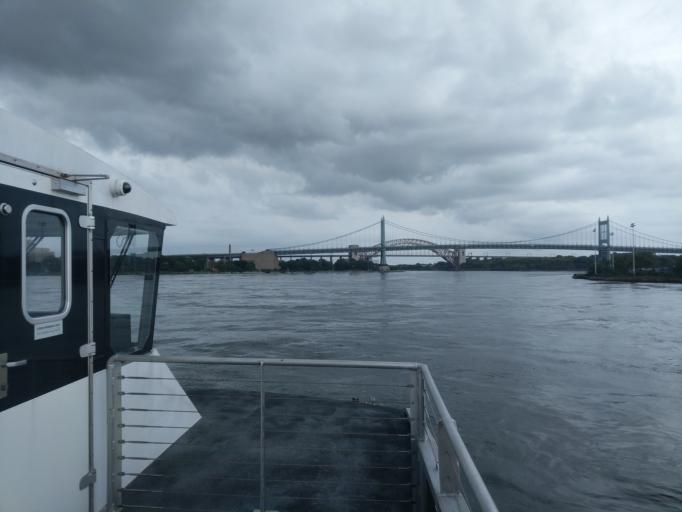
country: US
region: New York
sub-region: New York County
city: Manhattan
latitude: 40.7779
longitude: -73.9383
